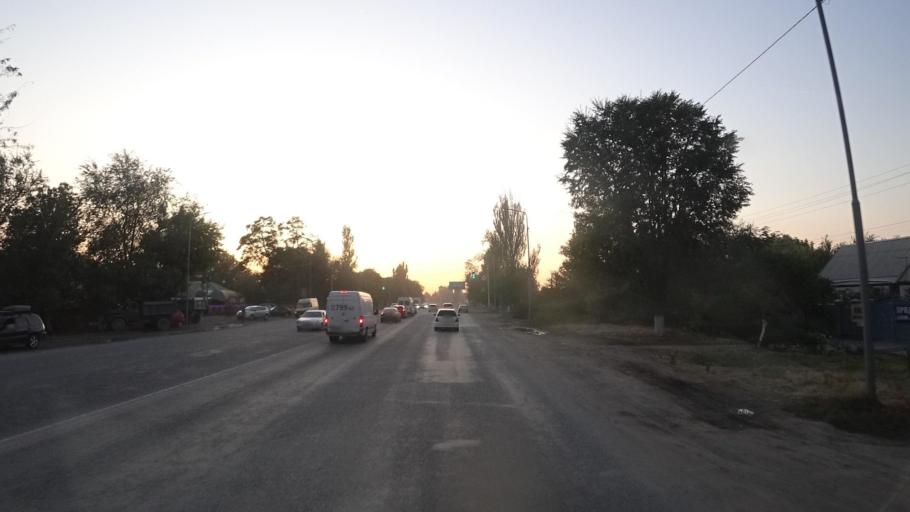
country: KG
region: Chuy
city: Lebedinovka
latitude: 42.8823
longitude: 74.6939
